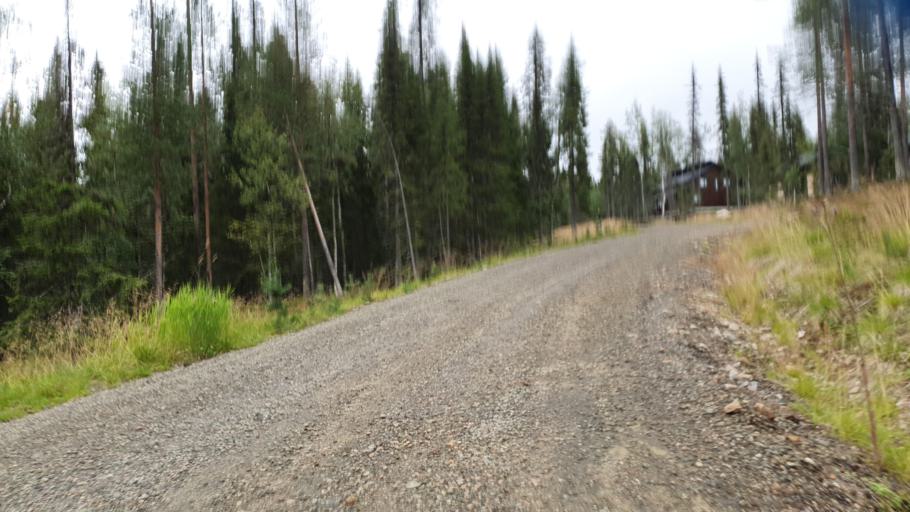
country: FI
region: Lapland
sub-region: Tunturi-Lappi
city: Kolari
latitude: 67.5988
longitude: 24.1974
